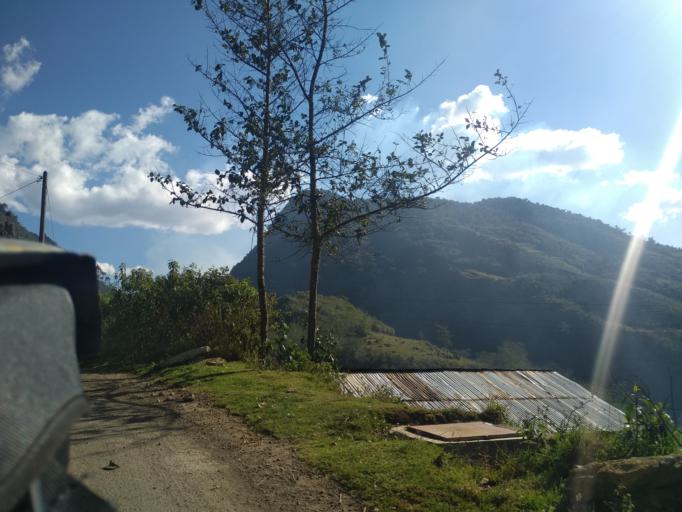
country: PE
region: Amazonas
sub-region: Provincia de Chachapoyas
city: Montevideo
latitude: -6.7164
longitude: -77.8206
